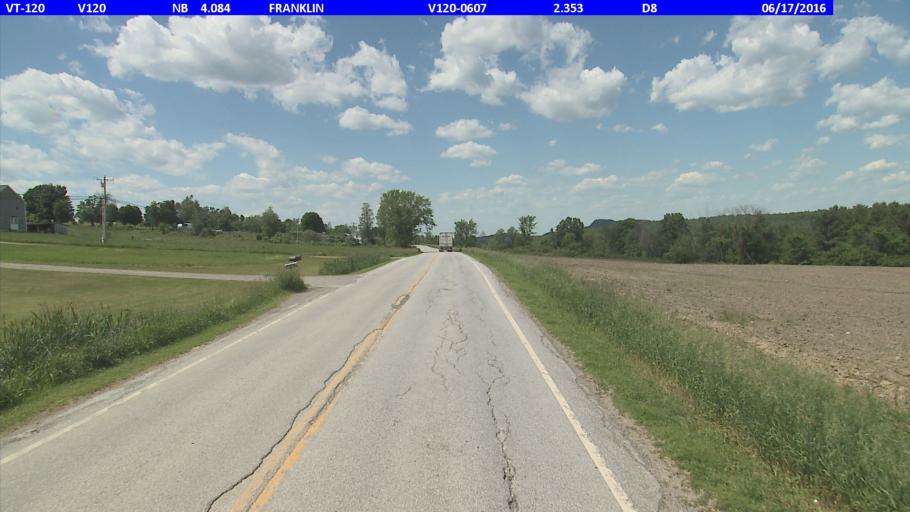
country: US
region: Vermont
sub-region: Franklin County
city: Enosburg Falls
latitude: 44.9668
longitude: -72.9080
